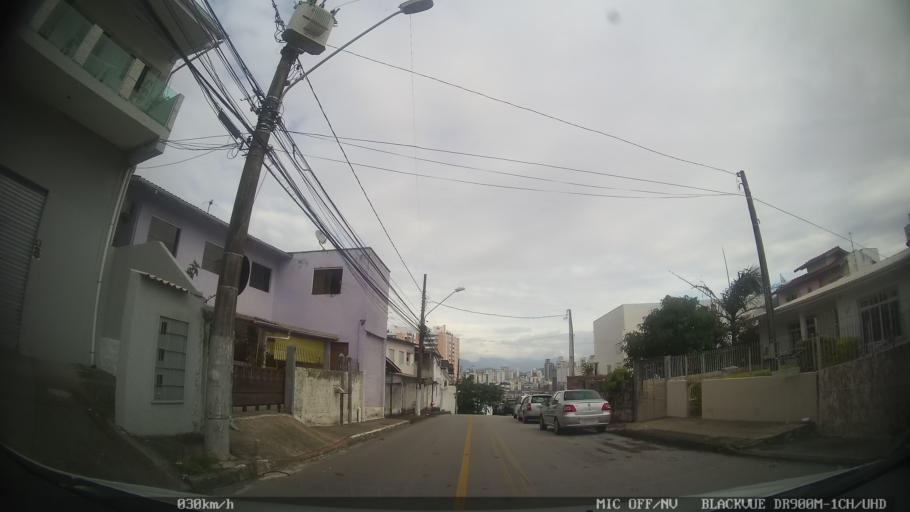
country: BR
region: Santa Catarina
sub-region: Sao Jose
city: Campinas
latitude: -27.5850
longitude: -48.6081
